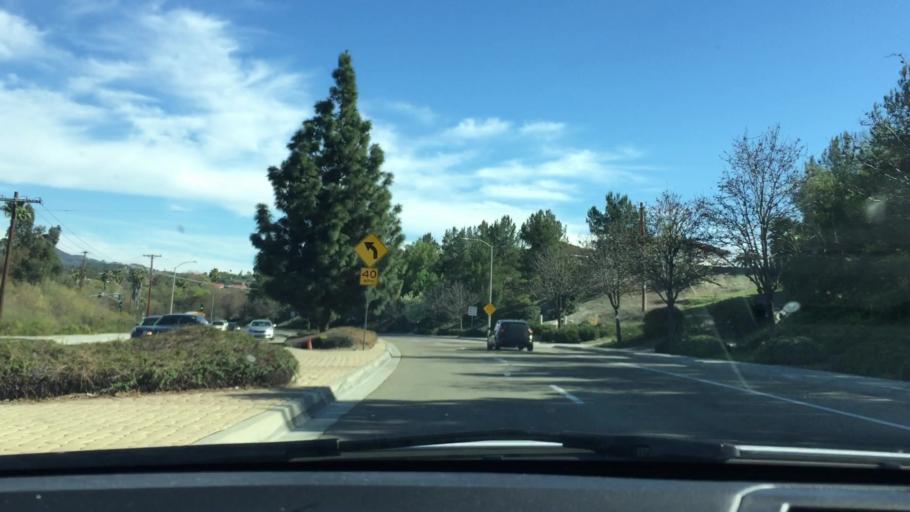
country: US
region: California
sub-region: San Diego County
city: Vista
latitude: 33.2367
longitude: -117.2642
